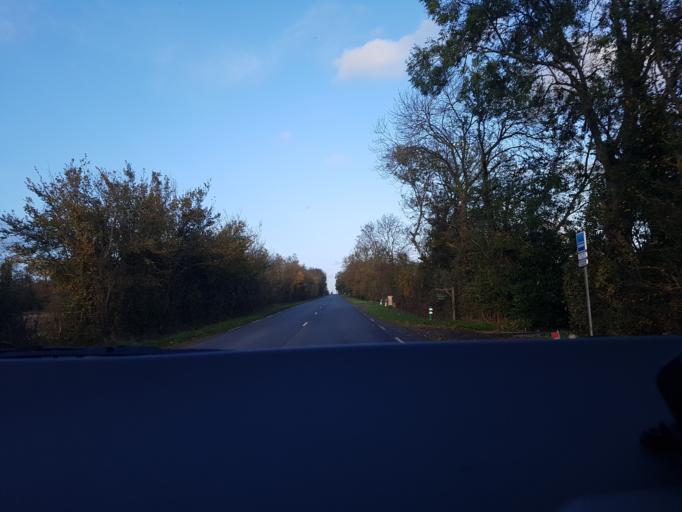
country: FR
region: Lower Normandy
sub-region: Departement du Calvados
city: Troarn
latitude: 49.2060
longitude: -0.1214
